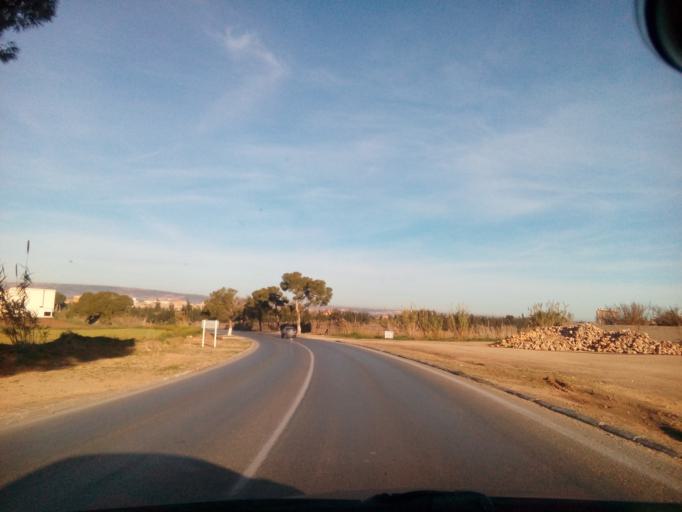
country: DZ
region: Mostaganem
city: Mostaganem
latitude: 35.7740
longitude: 0.1994
